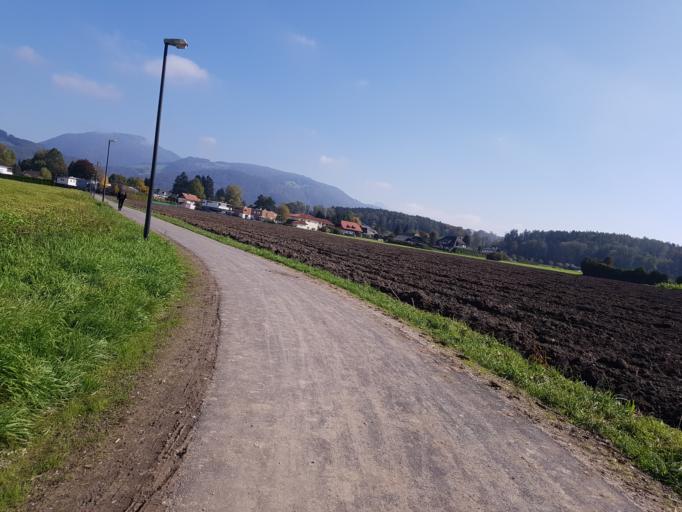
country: AT
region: Salzburg
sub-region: Salzburg Stadt
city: Salzburg
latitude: 47.7727
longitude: 13.0460
